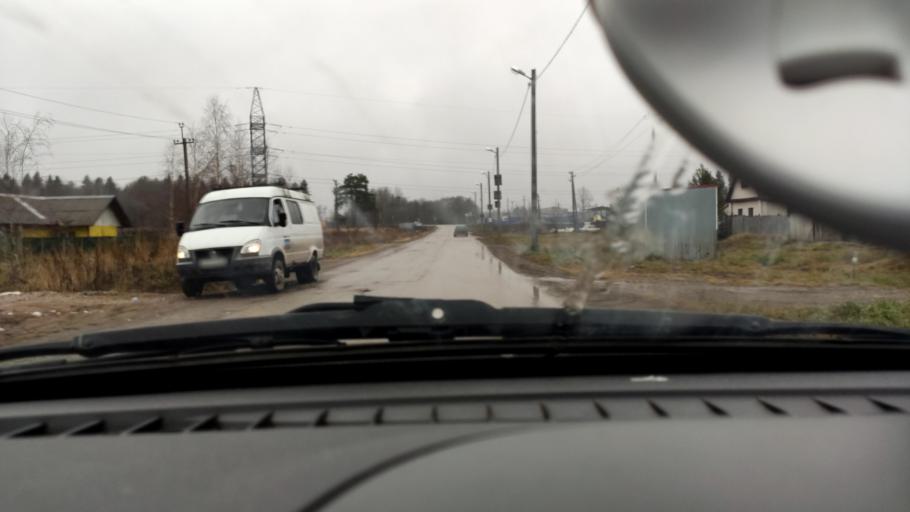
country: RU
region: Perm
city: Perm
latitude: 58.0402
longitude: 56.4082
